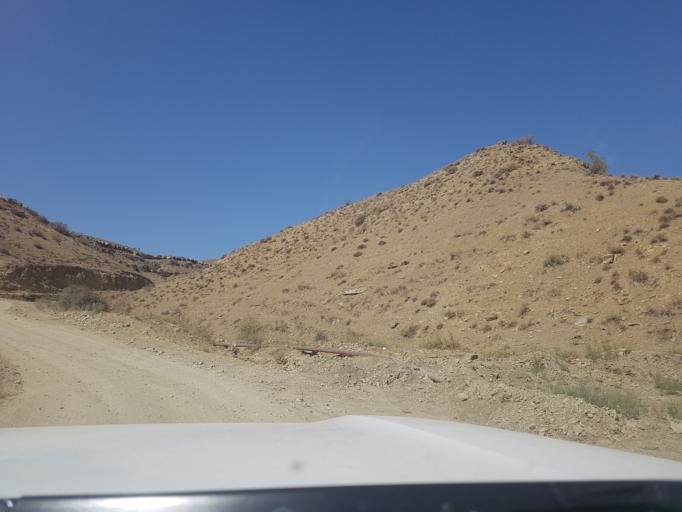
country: TM
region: Ahal
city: Baharly
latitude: 38.2398
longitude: 56.8912
